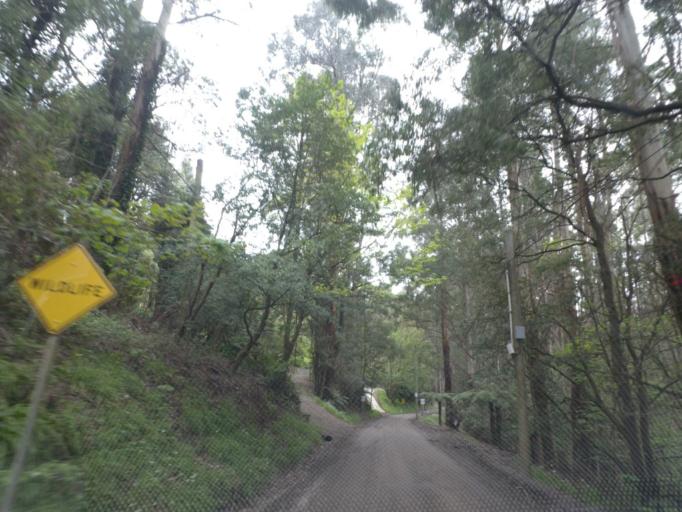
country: AU
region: Victoria
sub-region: Yarra Ranges
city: Olinda
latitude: -37.8504
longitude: 145.3610
